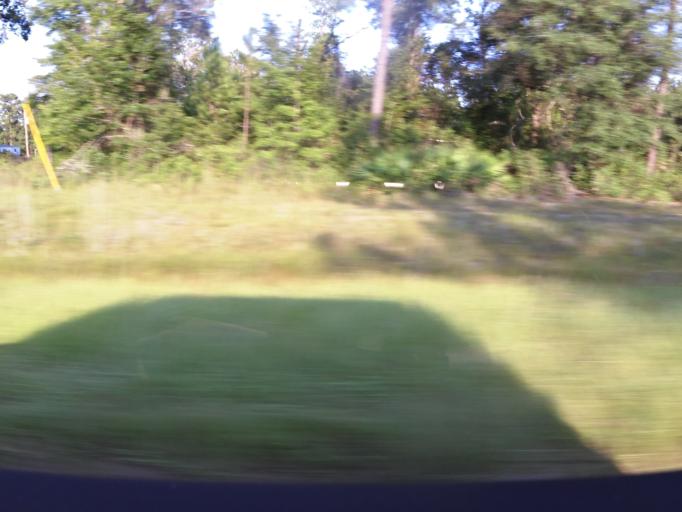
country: US
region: Florida
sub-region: Duval County
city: Baldwin
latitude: 30.4479
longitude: -82.0063
